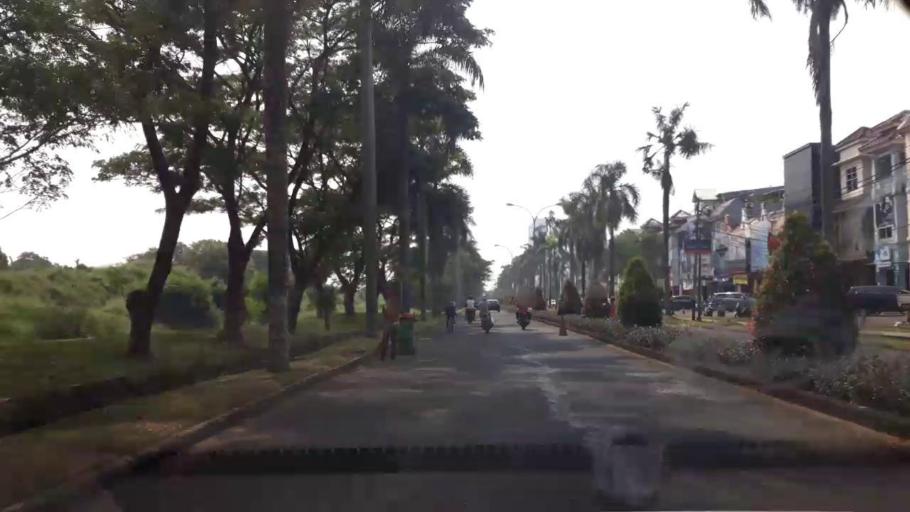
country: ID
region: Banten
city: Curug
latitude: -6.2238
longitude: 106.5889
